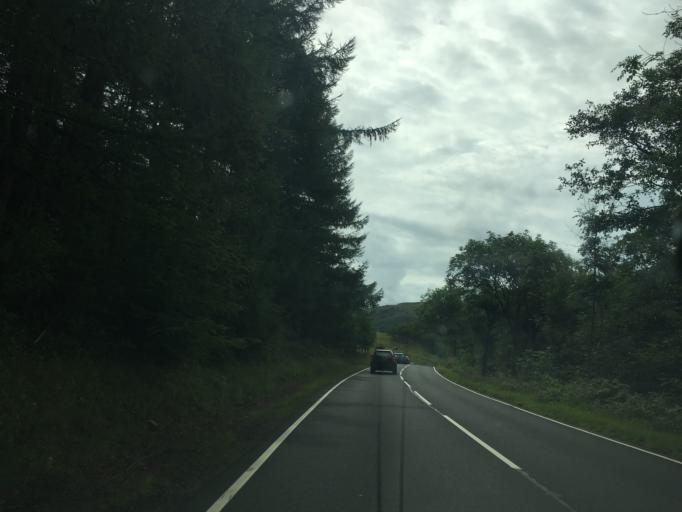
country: GB
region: Scotland
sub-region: Stirling
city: Callander
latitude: 56.2686
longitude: -4.2844
